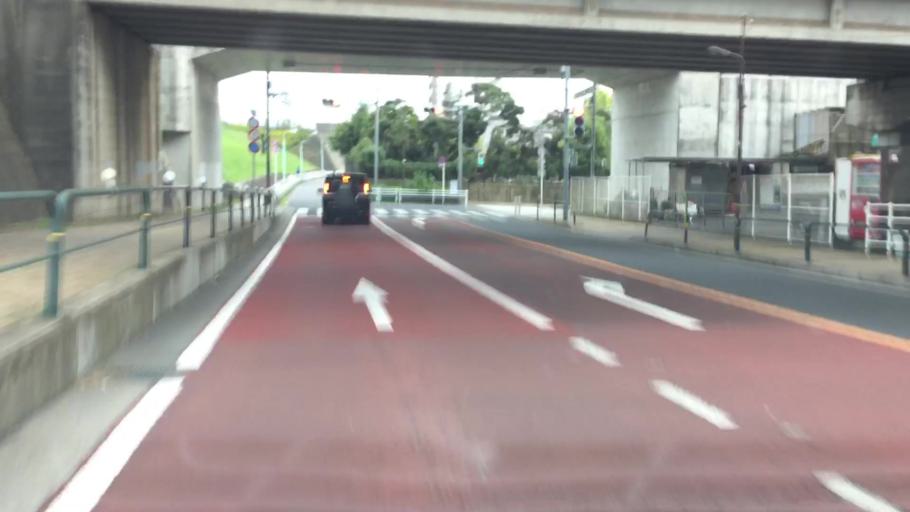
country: JP
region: Saitama
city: Soka
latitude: 35.7552
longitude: 139.8071
